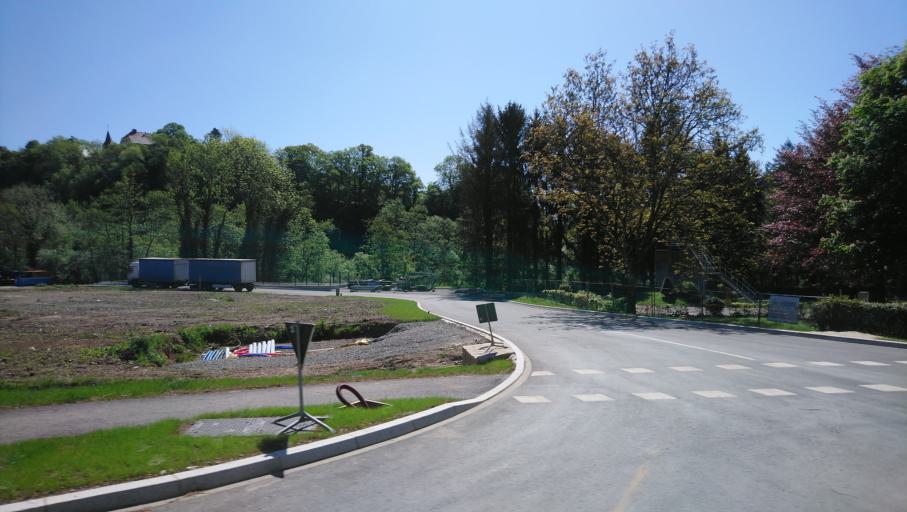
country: LU
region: Diekirch
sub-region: Canton de Vianden
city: Vianden
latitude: 49.9257
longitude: 6.2176
